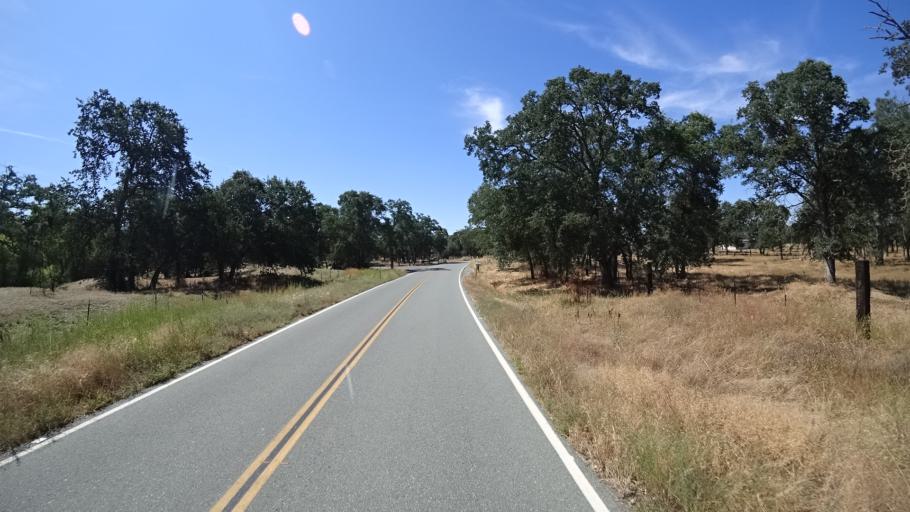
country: US
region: California
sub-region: Calaveras County
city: Rancho Calaveras
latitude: 38.1735
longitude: -120.9087
